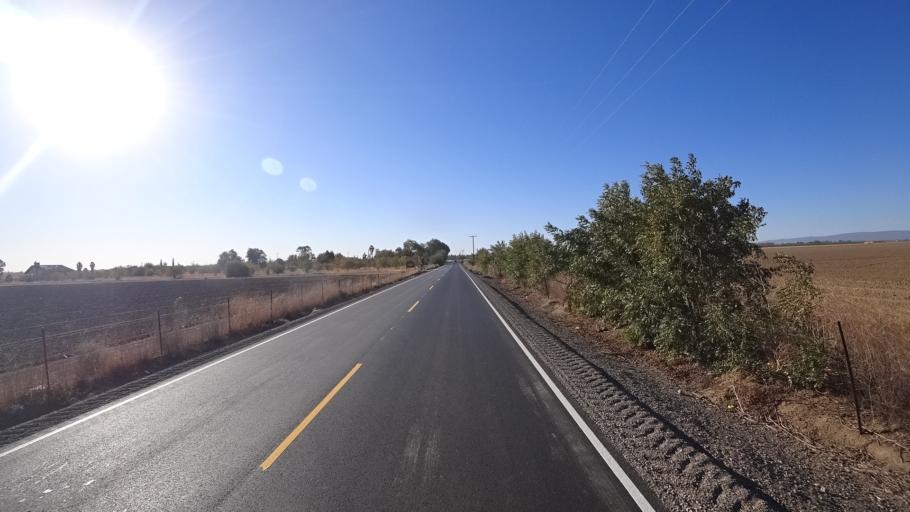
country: US
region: California
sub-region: Yolo County
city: Davis
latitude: 38.5695
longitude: -121.7861
